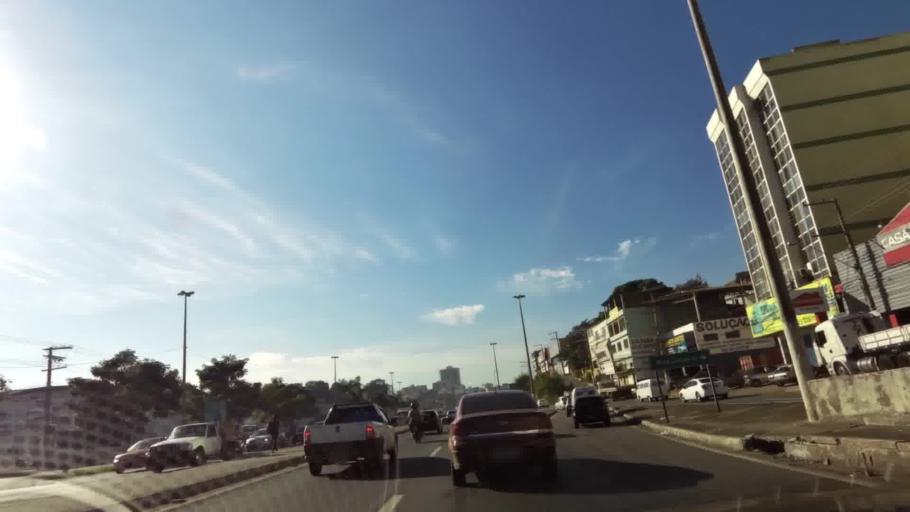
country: BR
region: Espirito Santo
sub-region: Vitoria
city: Vitoria
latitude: -20.3368
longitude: -40.3873
